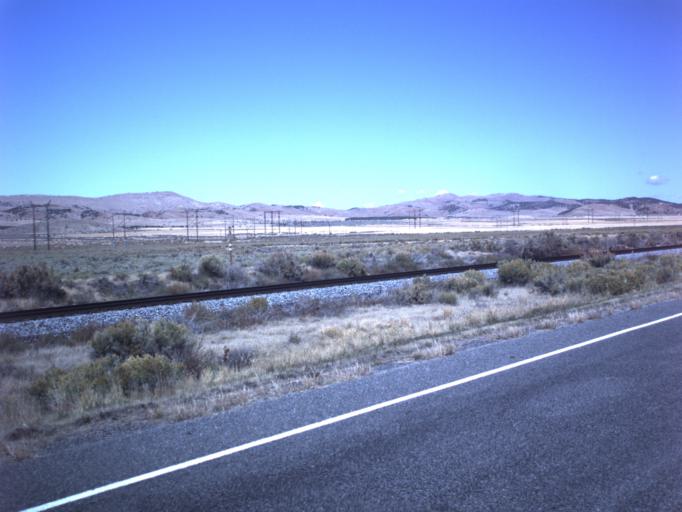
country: US
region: Utah
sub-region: Juab County
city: Nephi
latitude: 39.5357
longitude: -111.9304
